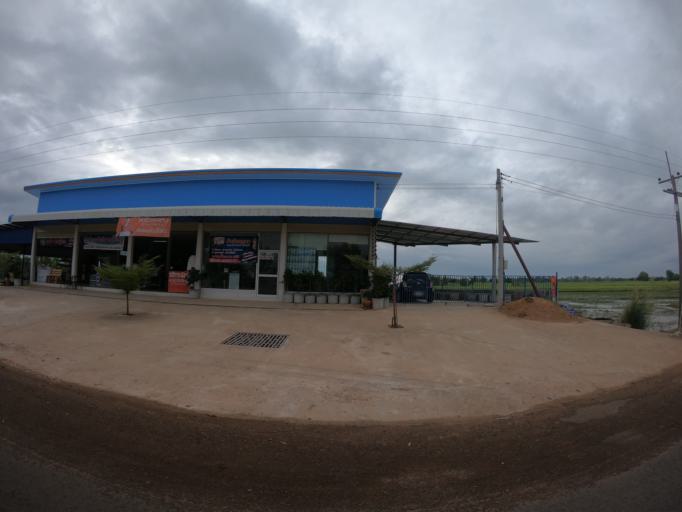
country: TH
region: Roi Et
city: Thawat Buri
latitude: 16.0945
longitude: 103.7851
